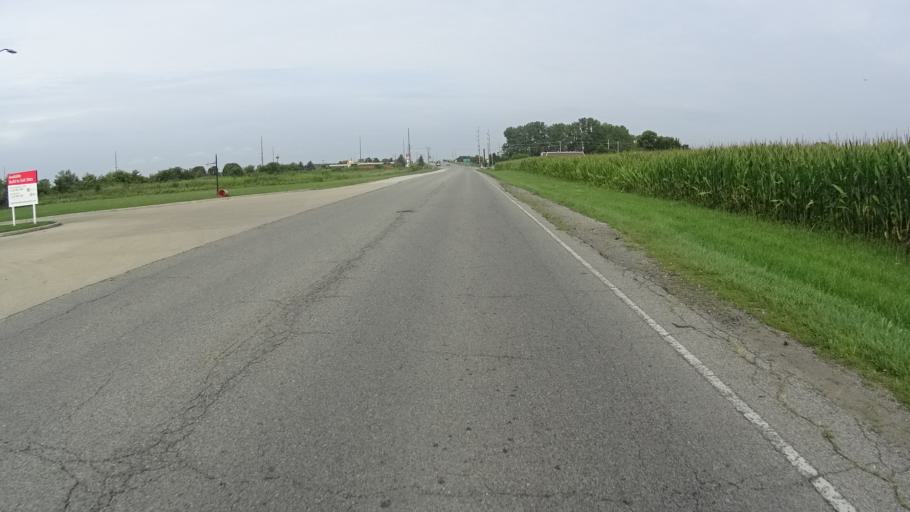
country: US
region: Indiana
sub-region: Madison County
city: Pendleton
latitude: 40.0040
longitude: -85.7647
